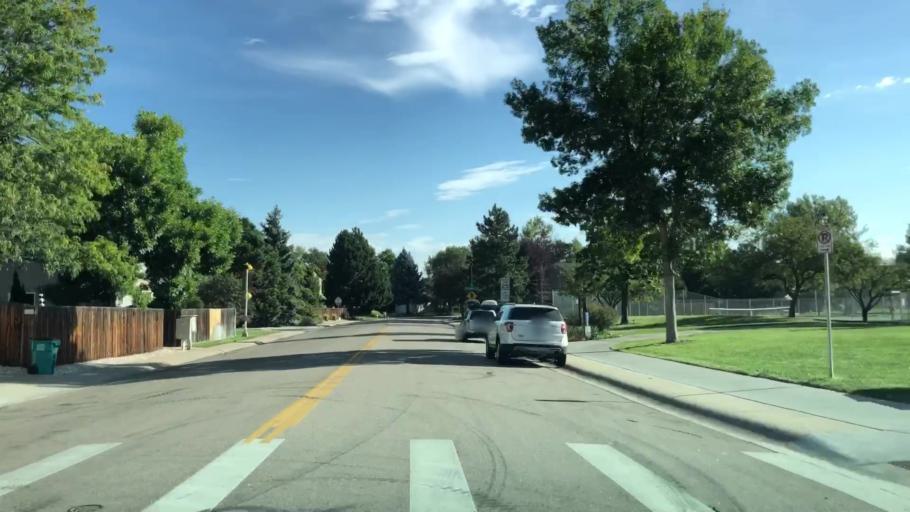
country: US
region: Colorado
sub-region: Larimer County
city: Fort Collins
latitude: 40.5272
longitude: -105.0483
